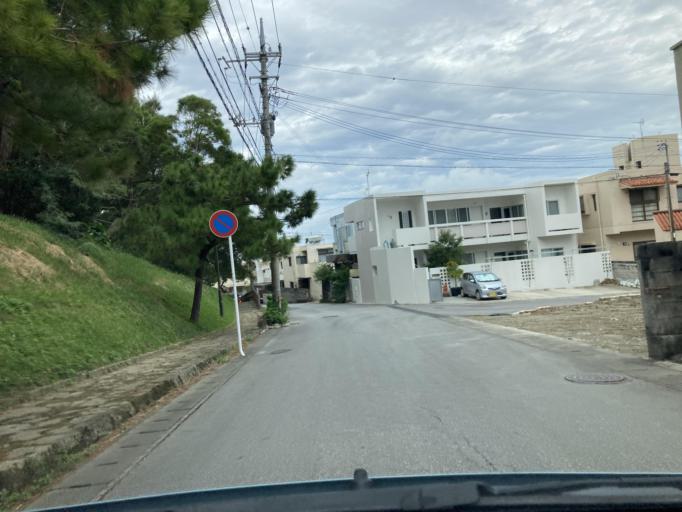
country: JP
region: Okinawa
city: Naha-shi
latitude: 26.2184
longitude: 127.7320
